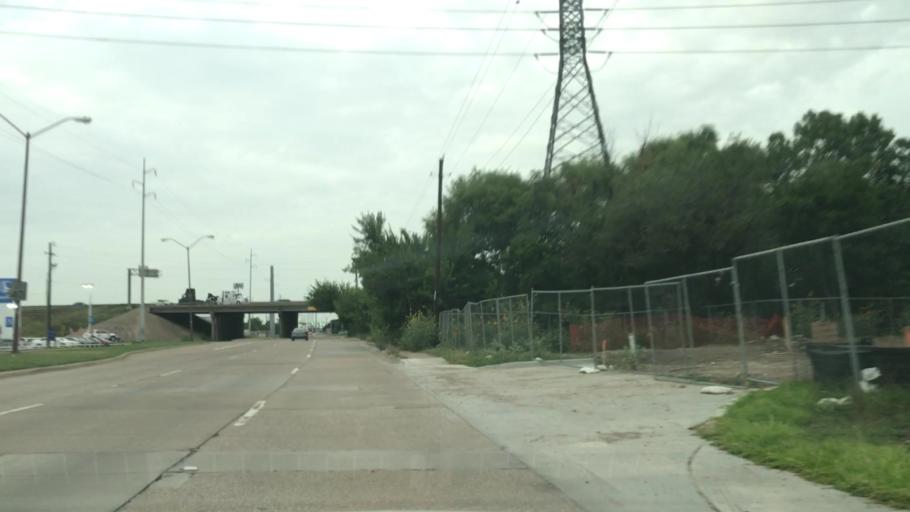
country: US
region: Texas
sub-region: Dallas County
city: Garland
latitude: 32.8648
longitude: -96.6656
